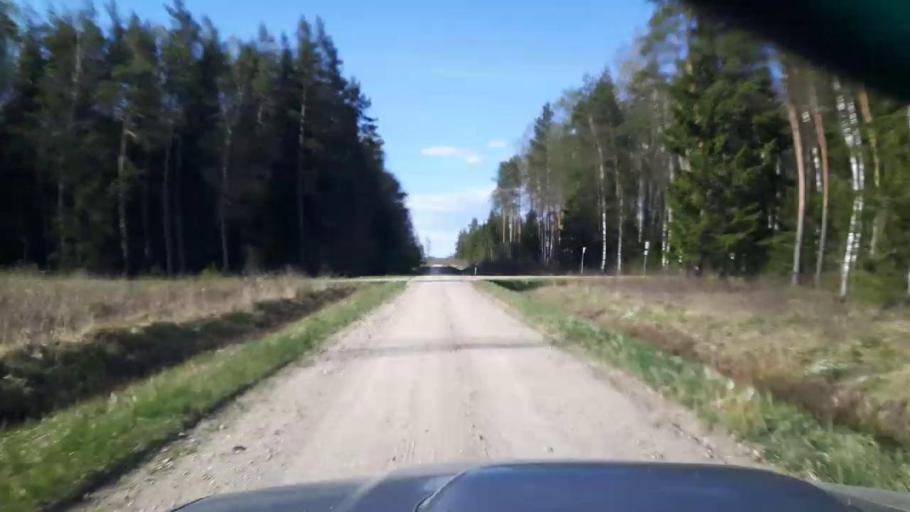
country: EE
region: Paernumaa
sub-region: Tootsi vald
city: Tootsi
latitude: 58.4275
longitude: 24.8513
